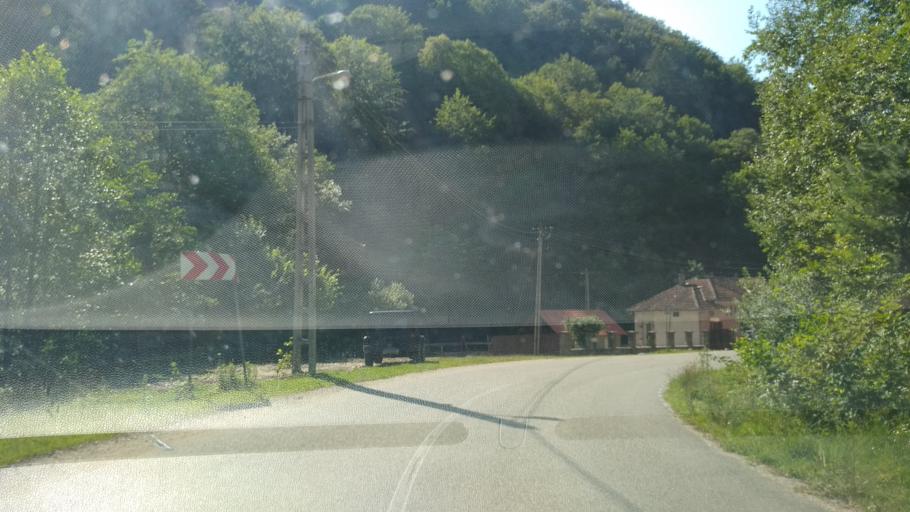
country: RO
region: Hunedoara
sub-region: Comuna Orastioara de Sus
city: Orastioara de Sus
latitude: 45.6279
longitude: 23.2193
